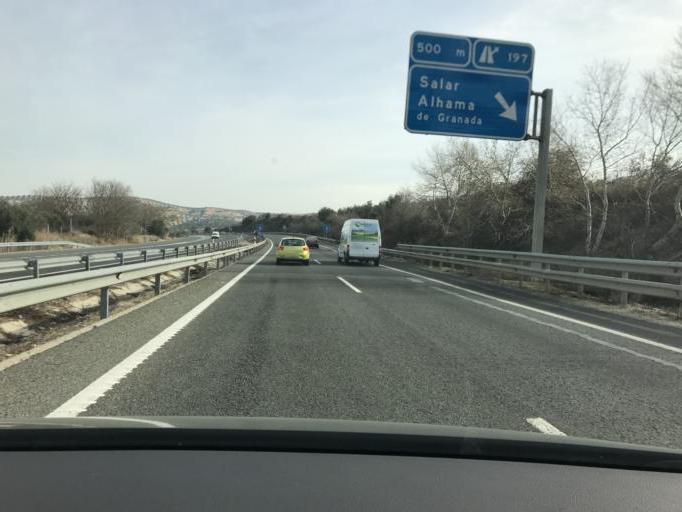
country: ES
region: Andalusia
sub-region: Provincia de Granada
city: Salar
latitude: 37.1661
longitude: -4.0921
